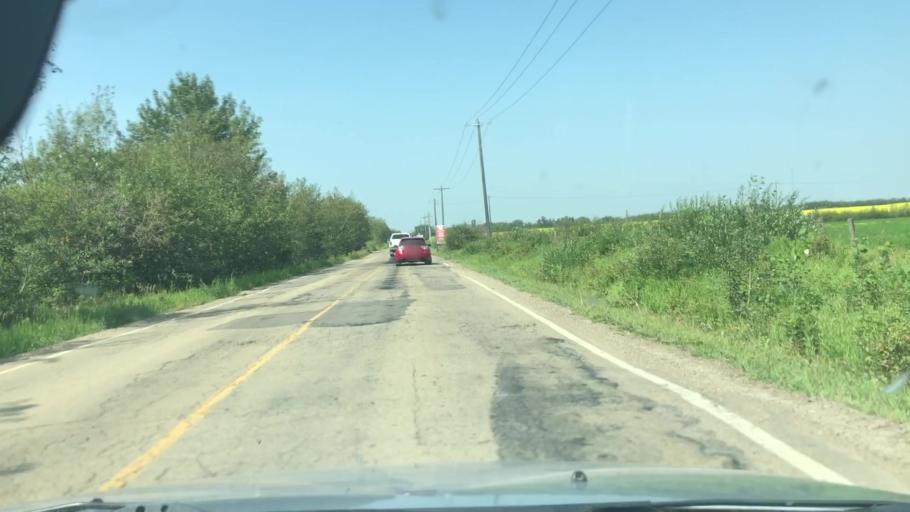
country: CA
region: Alberta
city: St. Albert
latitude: 53.5122
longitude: -113.7101
